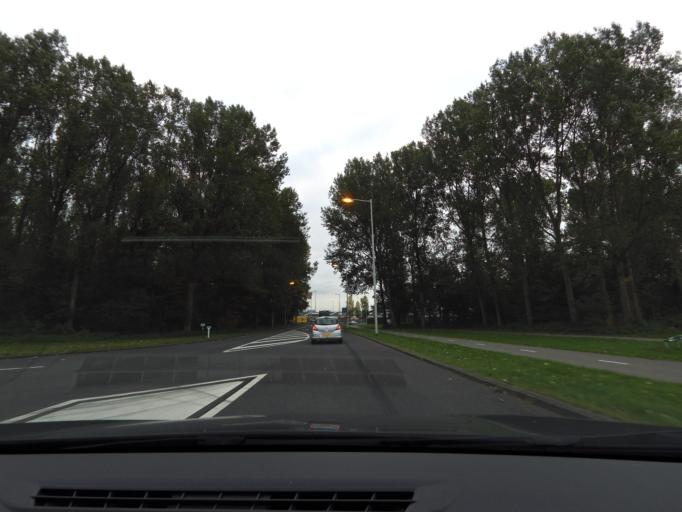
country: NL
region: South Holland
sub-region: Gemeente Maassluis
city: Maassluis
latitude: 51.8912
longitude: 4.2301
